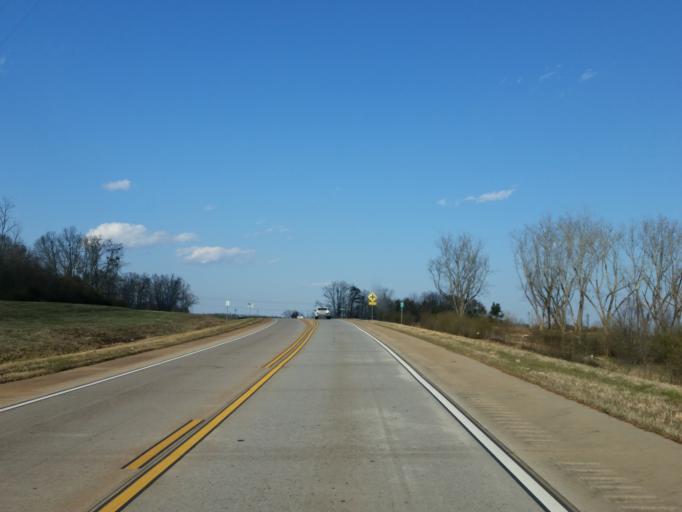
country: US
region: Georgia
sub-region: Lamar County
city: Barnesville
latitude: 33.0394
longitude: -84.1350
